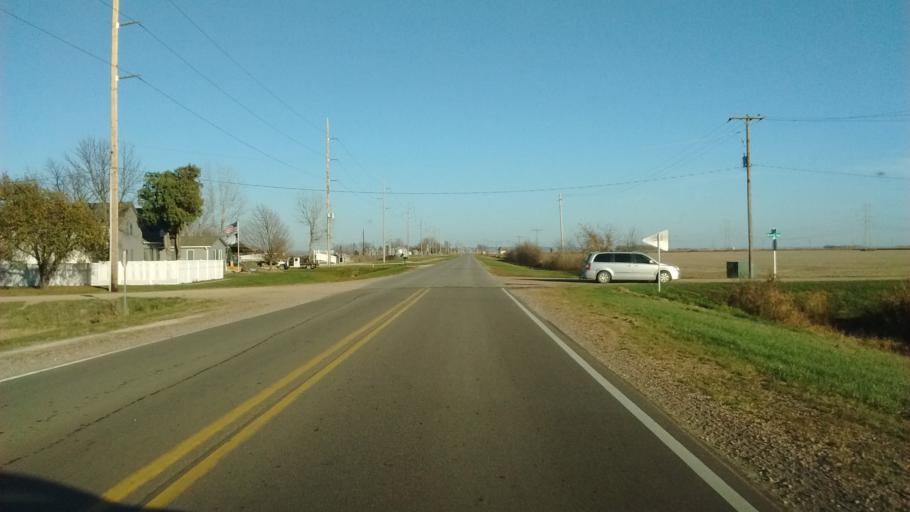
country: US
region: Iowa
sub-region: Woodbury County
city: Sergeant Bluff
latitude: 42.3302
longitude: -96.3109
